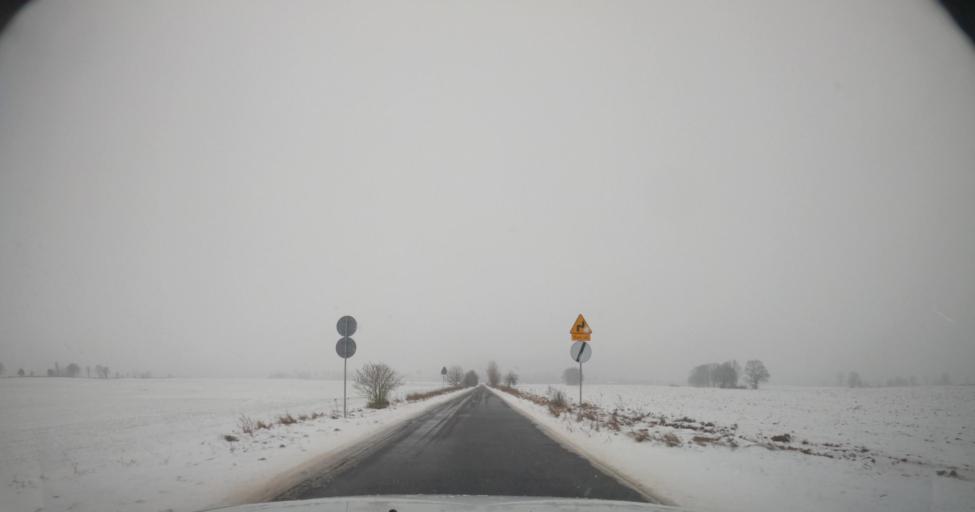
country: PL
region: West Pomeranian Voivodeship
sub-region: Powiat gryficki
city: Brojce
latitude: 53.8897
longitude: 15.3867
